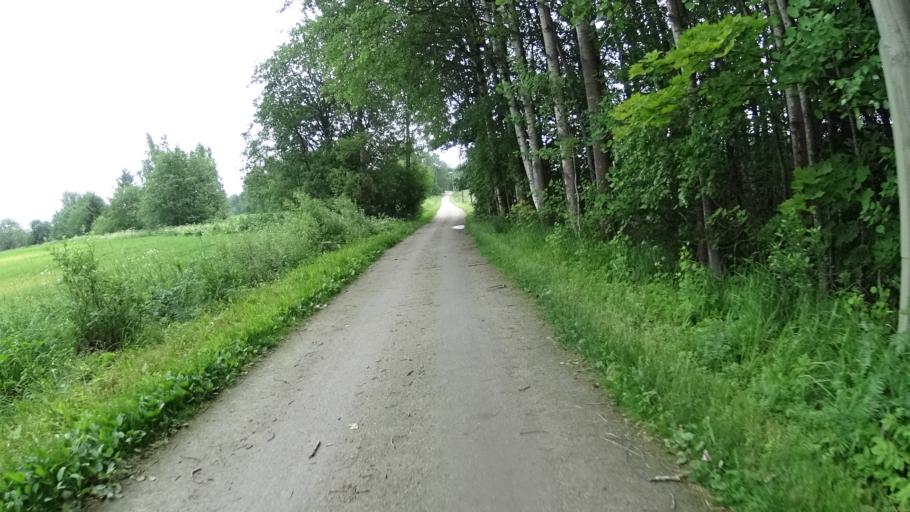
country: FI
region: Uusimaa
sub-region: Helsinki
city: Helsinki
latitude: 60.2663
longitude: 24.9345
